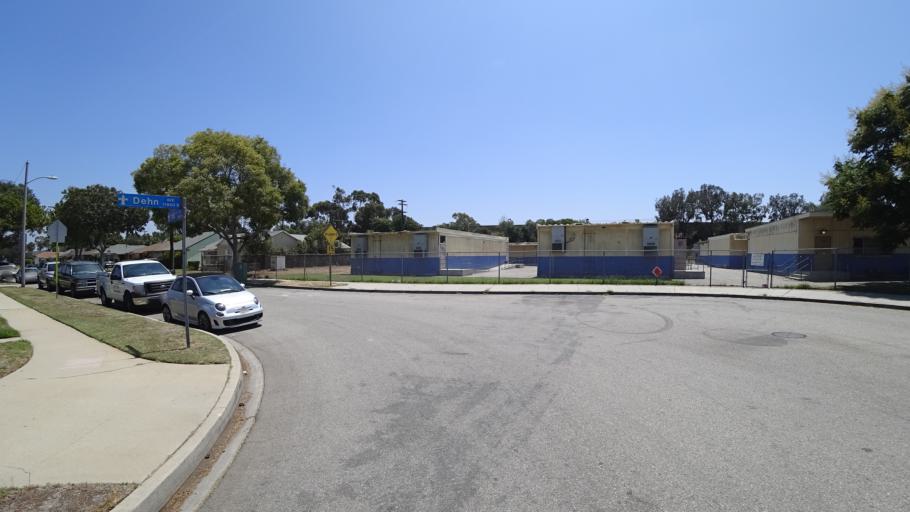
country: US
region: California
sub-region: Los Angeles County
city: Hawthorne
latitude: 33.9262
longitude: -118.3320
